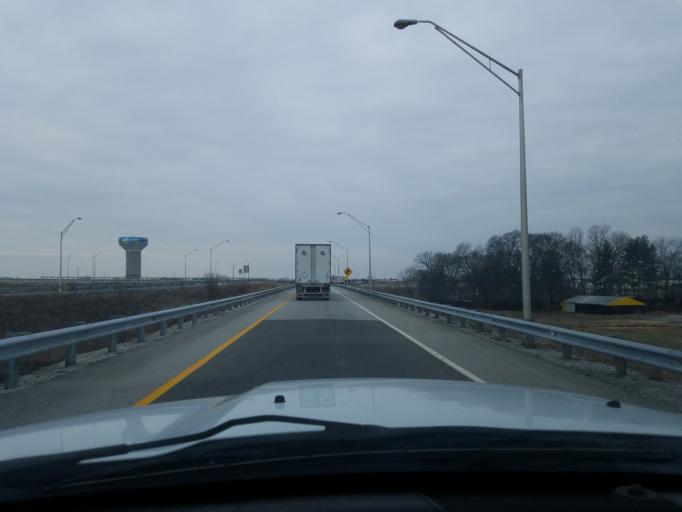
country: US
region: Kentucky
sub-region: Warren County
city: Plano
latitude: 36.9128
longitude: -86.4320
